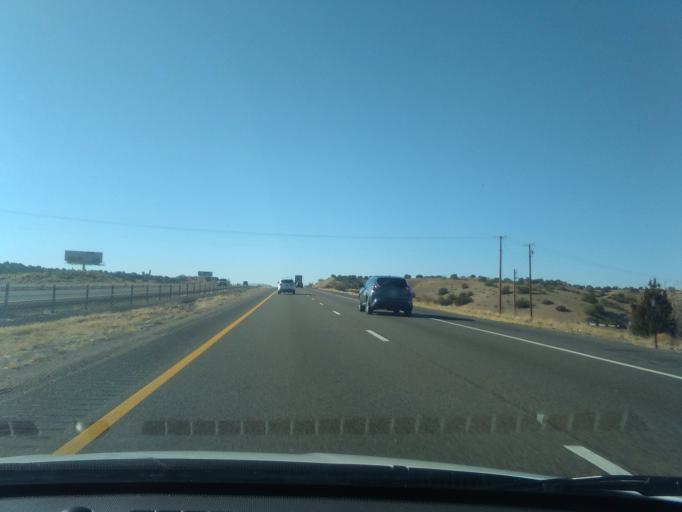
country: US
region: New Mexico
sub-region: Sandoval County
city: San Felipe Pueblo
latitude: 35.3701
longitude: -106.4802
